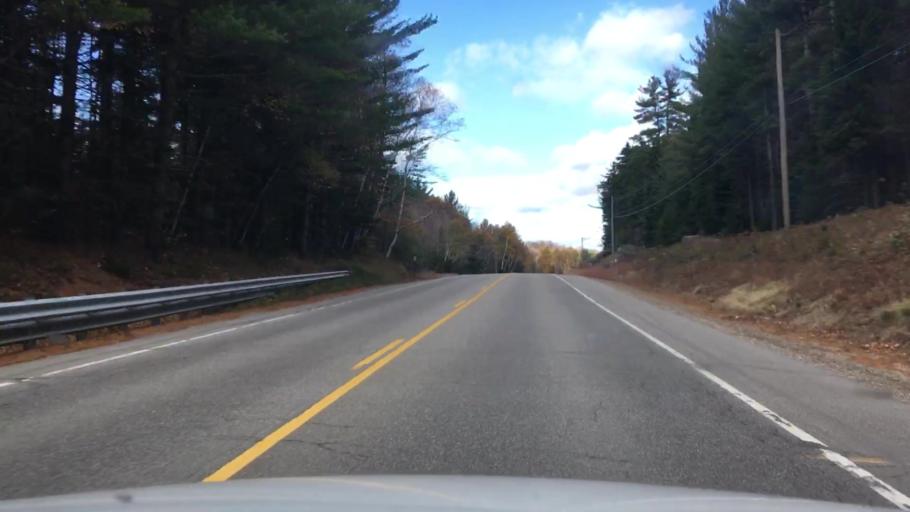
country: US
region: New Hampshire
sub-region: Coos County
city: Gorham
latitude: 44.2965
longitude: -71.2244
